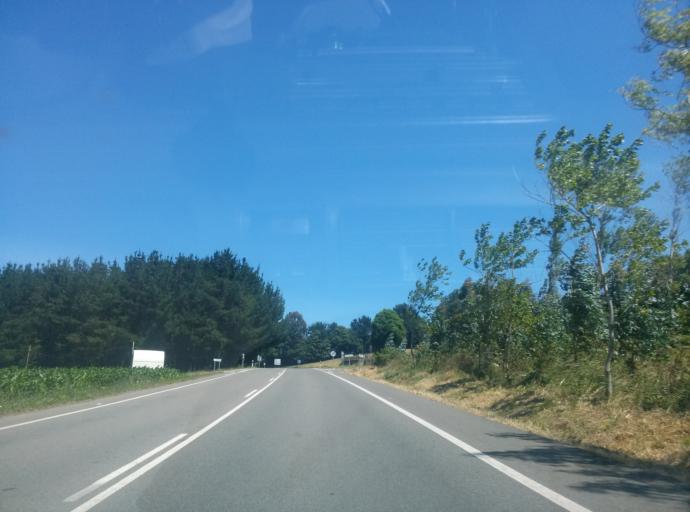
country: ES
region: Galicia
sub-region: Provincia de Lugo
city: Meira
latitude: 43.2307
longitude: -7.3456
